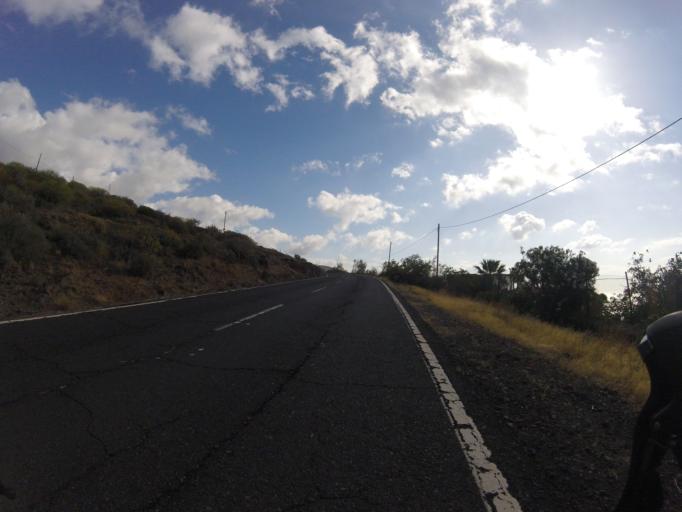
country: ES
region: Canary Islands
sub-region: Provincia de Santa Cruz de Tenerife
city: Candelaria
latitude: 28.3927
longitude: -16.3513
